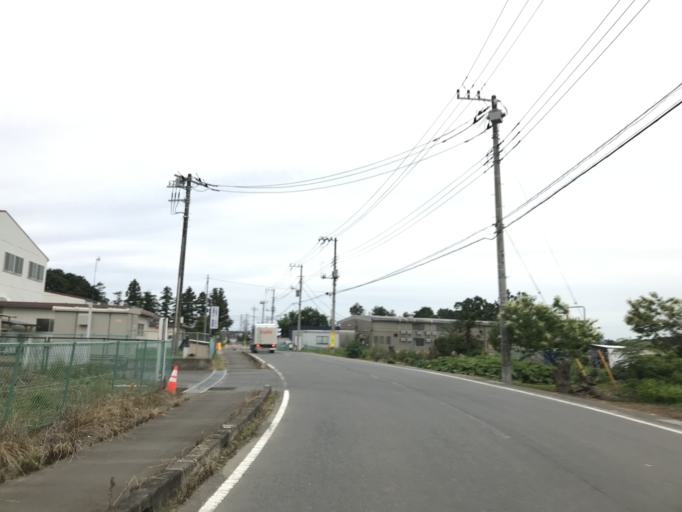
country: JP
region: Ibaraki
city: Ishioka
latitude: 36.2184
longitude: 140.2968
